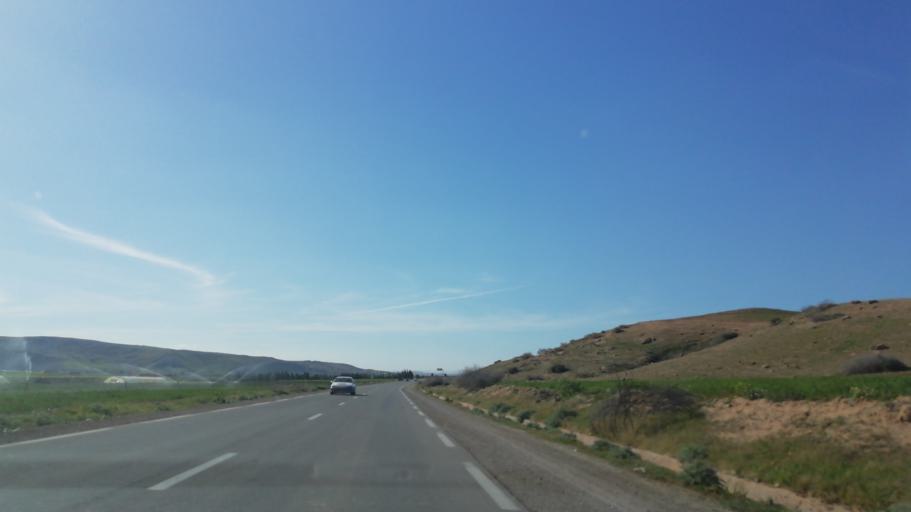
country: DZ
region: Mascara
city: Oued el Abtal
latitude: 35.4497
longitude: 0.7902
